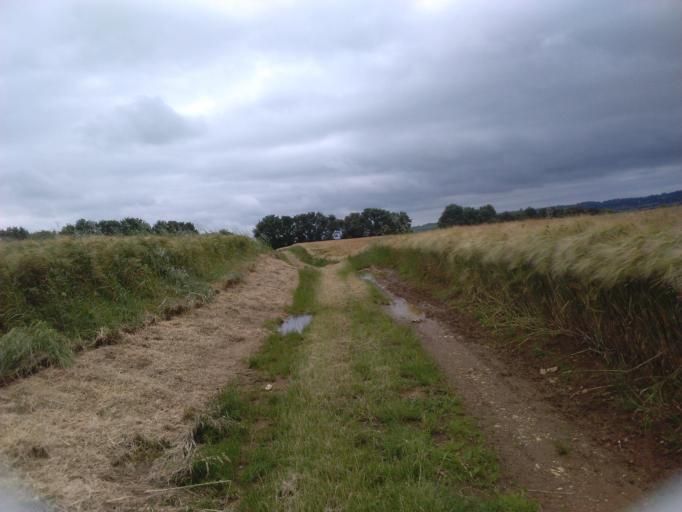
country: FR
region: Centre
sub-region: Departement du Cher
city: Sancerre
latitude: 47.3127
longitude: 2.7235
